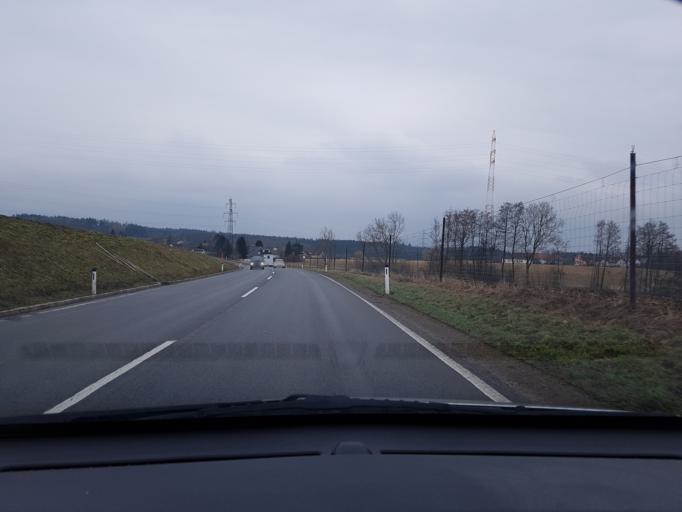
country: AT
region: Upper Austria
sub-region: Steyr Stadt
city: Steyr
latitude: 48.0746
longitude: 14.3815
